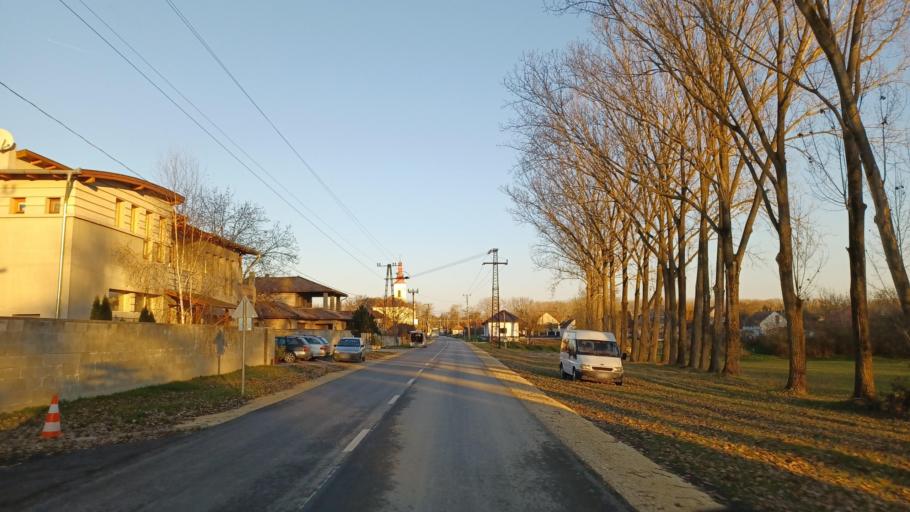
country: HU
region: Bacs-Kiskun
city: Batya
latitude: 46.4925
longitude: 18.8988
